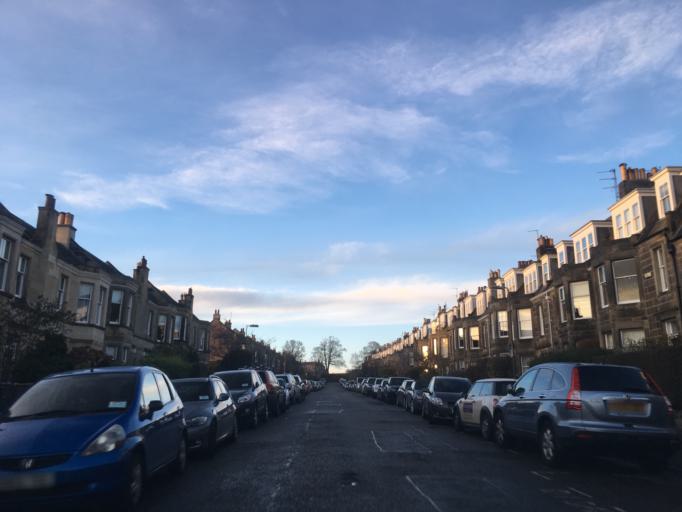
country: GB
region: Scotland
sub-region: Edinburgh
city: Colinton
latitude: 55.9470
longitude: -3.2395
